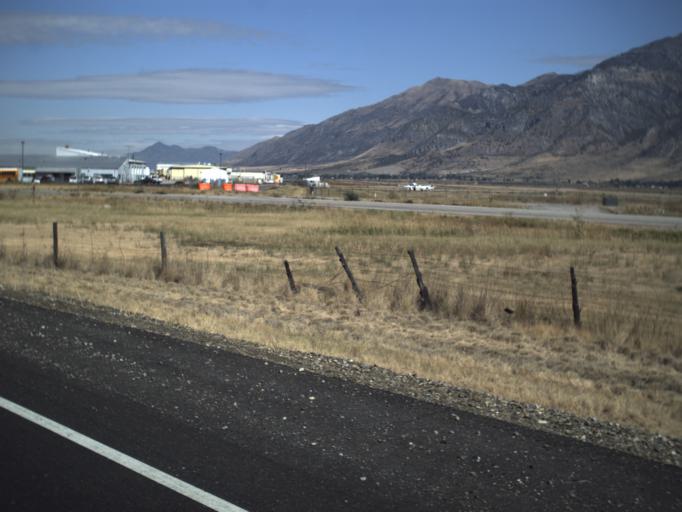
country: US
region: Utah
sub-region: Box Elder County
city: Brigham City
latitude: 41.5363
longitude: -112.0644
